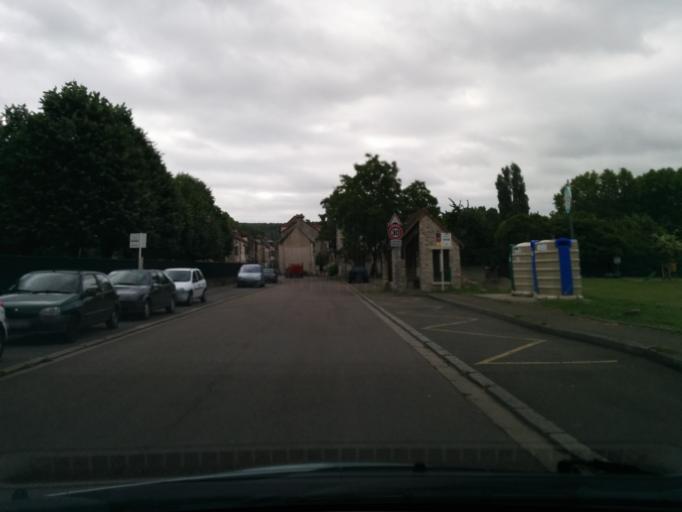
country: FR
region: Ile-de-France
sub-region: Departement des Yvelines
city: Follainville-Dennemont
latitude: 49.0120
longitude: 1.6966
